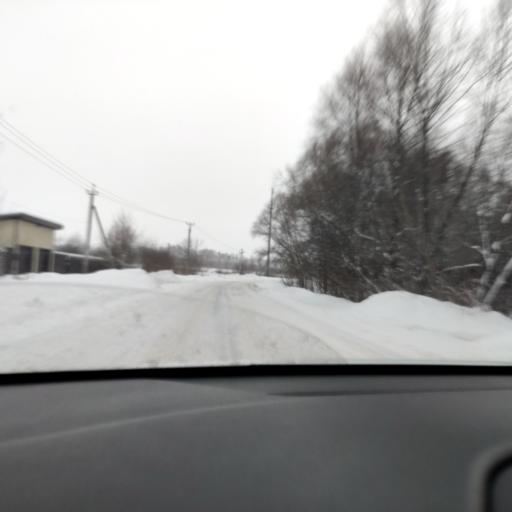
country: RU
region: Tatarstan
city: Vysokaya Gora
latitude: 55.9571
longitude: 49.1584
